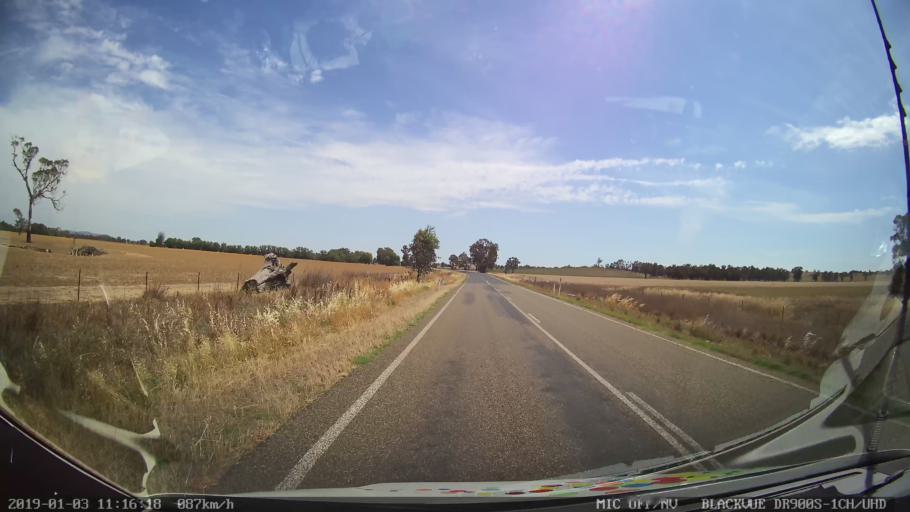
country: AU
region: New South Wales
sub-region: Young
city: Young
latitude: -34.1535
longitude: 148.2695
